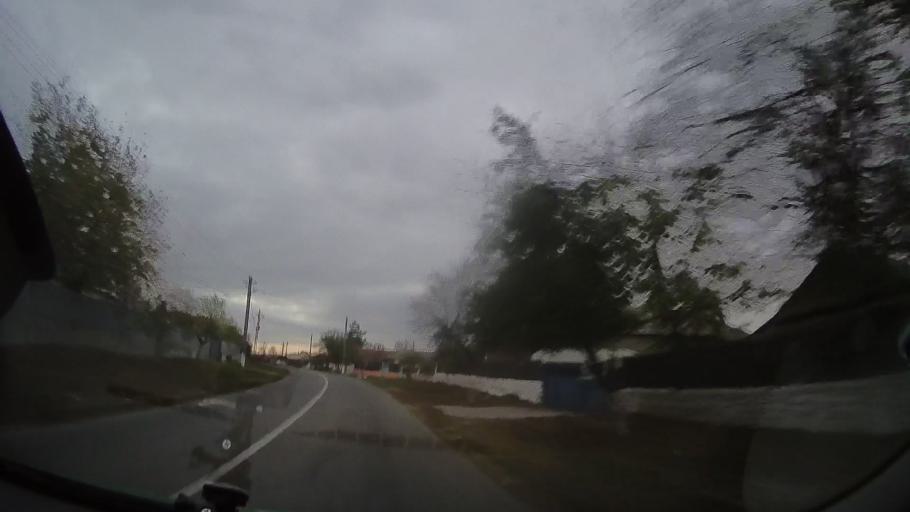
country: RO
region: Tulcea
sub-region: Comuna Mihai Bravu
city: Turda
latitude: 44.9716
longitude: 28.6273
